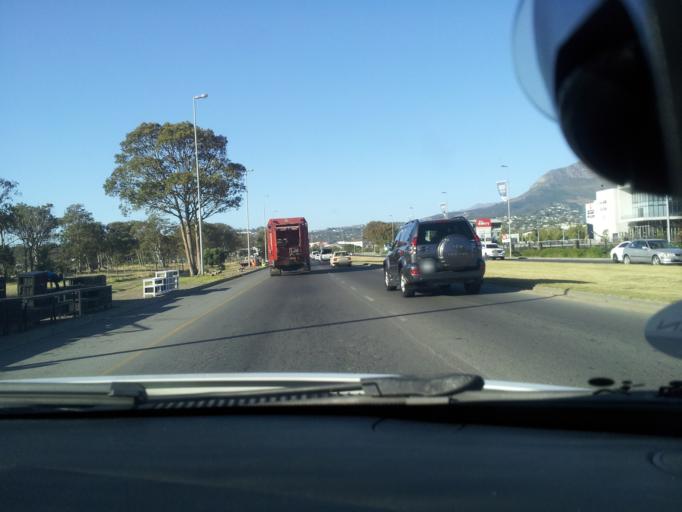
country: ZA
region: Western Cape
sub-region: Cape Winelands District Municipality
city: Stellenbosch
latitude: -34.0892
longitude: 18.8192
